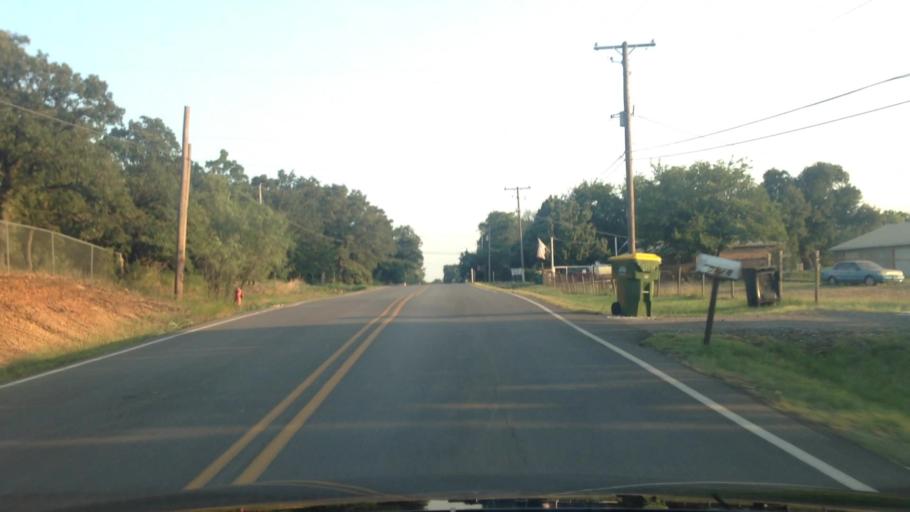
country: US
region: Texas
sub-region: Tarrant County
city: Rendon
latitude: 32.6039
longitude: -97.2154
